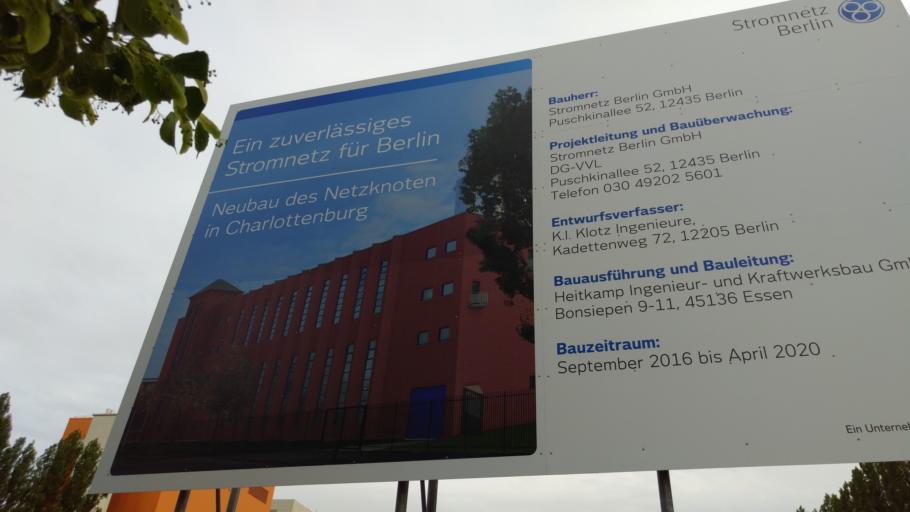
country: DE
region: Berlin
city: Charlottenburg-Nord
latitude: 52.5232
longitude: 13.3074
